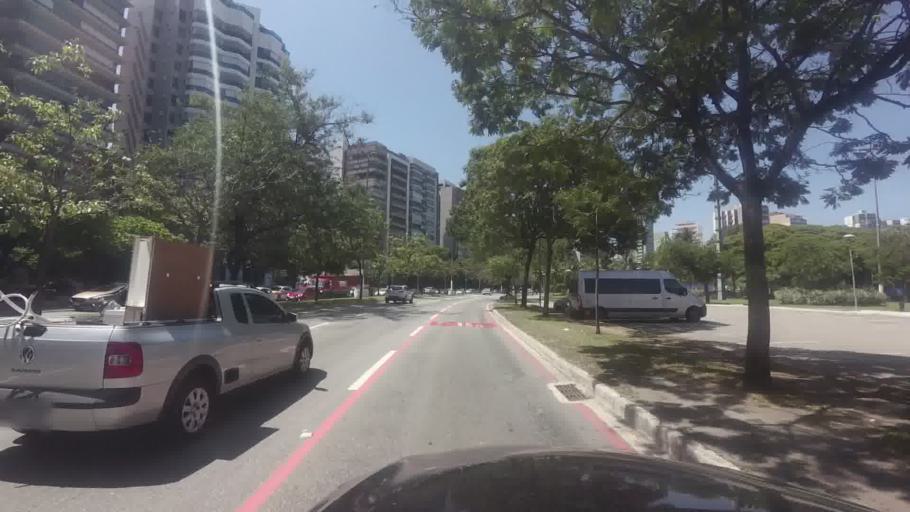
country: BR
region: Espirito Santo
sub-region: Vila Velha
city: Vila Velha
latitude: -20.3005
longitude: -40.2920
